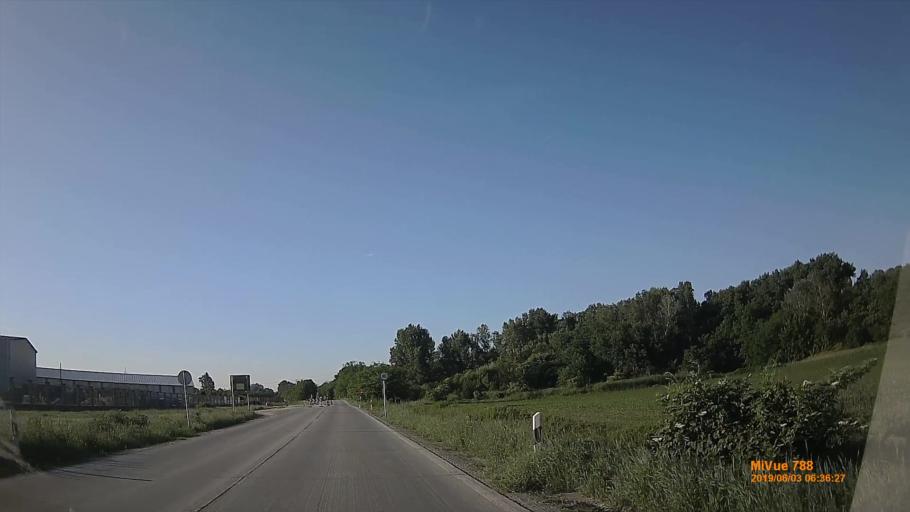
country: HU
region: Pest
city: Taksony
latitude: 47.3081
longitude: 19.0817
